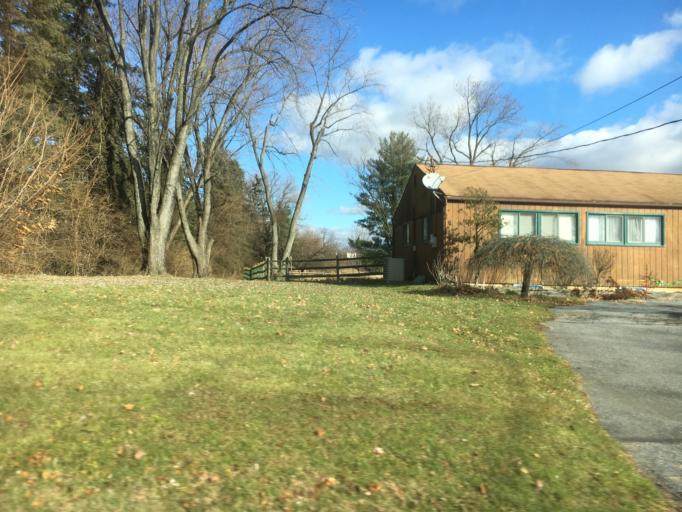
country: US
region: Pennsylvania
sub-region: Lehigh County
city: Egypt
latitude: 40.6835
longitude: -75.5423
